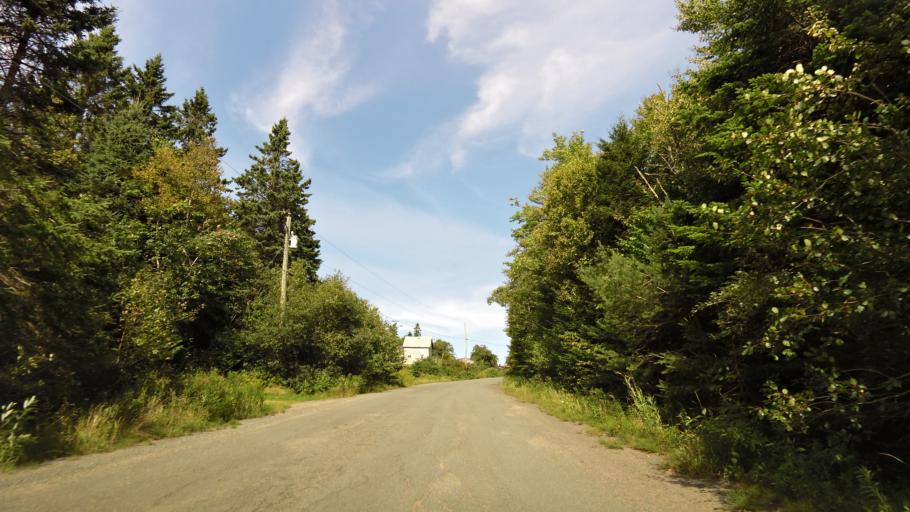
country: CA
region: New Brunswick
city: Hampton
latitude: 45.5631
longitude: -65.8438
